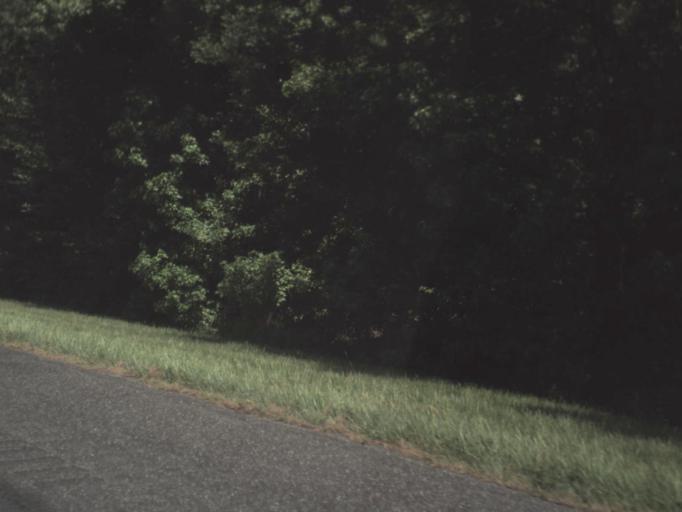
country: US
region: Florida
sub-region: Madison County
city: Madison
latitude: 30.4319
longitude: -83.5489
